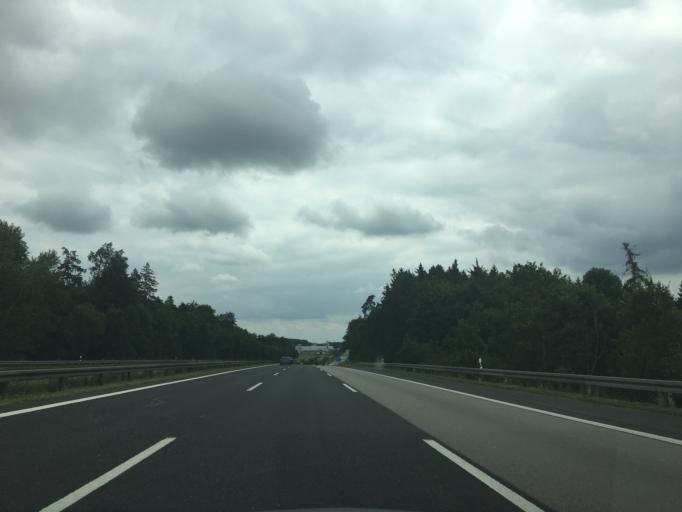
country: DE
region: Bavaria
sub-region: Upper Bavaria
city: Denkendorf
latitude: 48.9420
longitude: 11.4472
